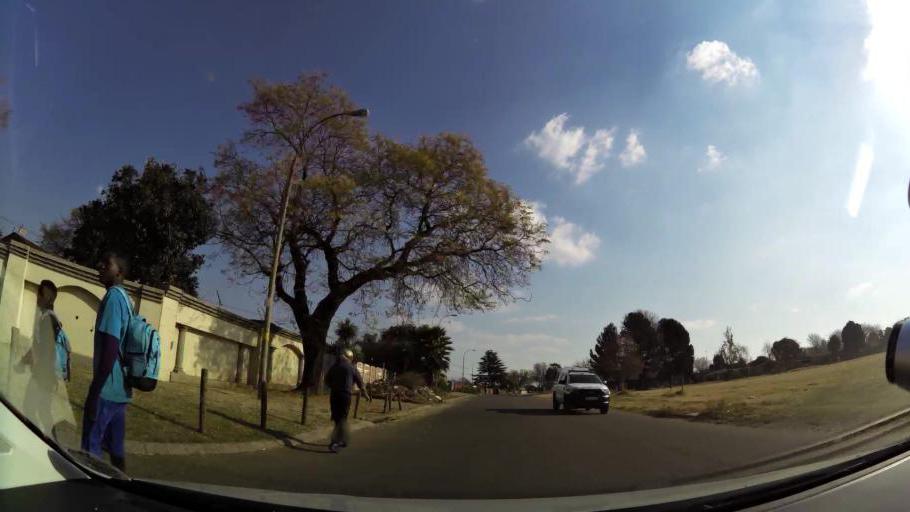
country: ZA
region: Gauteng
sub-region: City of Johannesburg Metropolitan Municipality
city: Modderfontein
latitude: -26.0872
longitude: 28.1954
